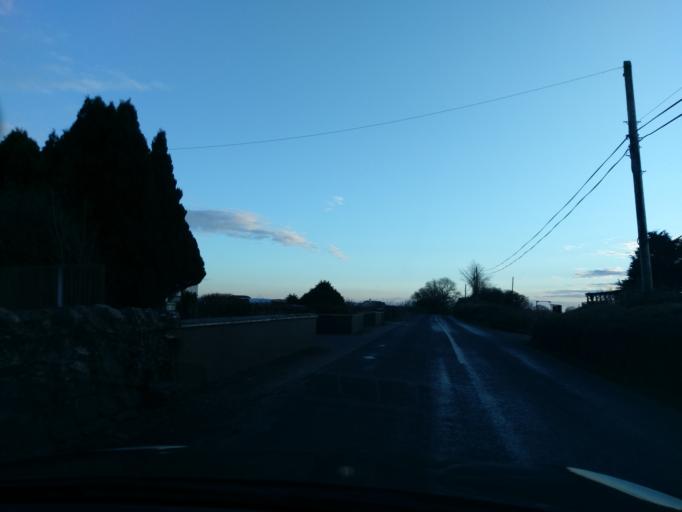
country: IE
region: Connaught
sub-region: County Galway
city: Athenry
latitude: 53.3065
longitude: -8.6215
